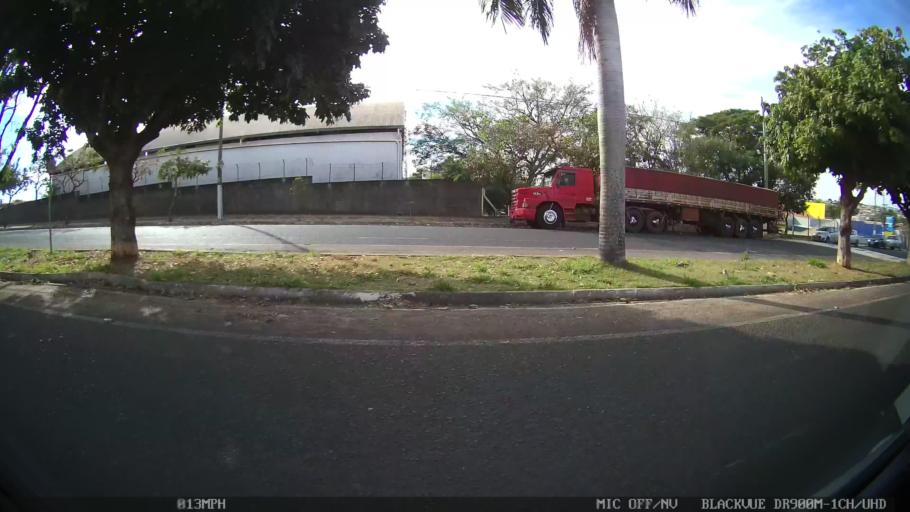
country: BR
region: Sao Paulo
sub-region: Catanduva
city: Catanduva
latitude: -21.1321
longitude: -48.9954
